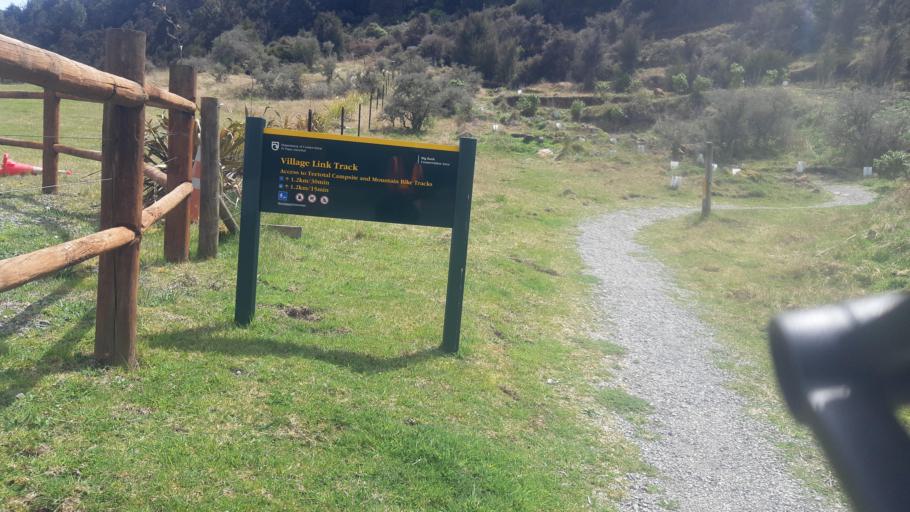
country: NZ
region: Tasman
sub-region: Tasman District
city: Wakefield
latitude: -41.7986
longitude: 172.8448
